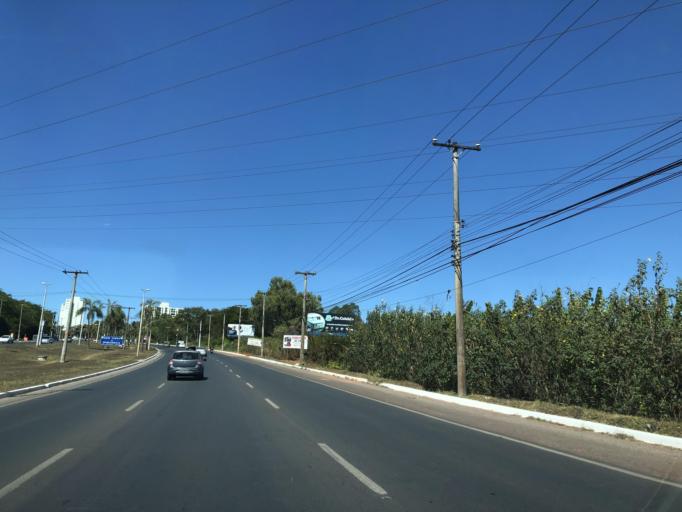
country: BR
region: Federal District
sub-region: Brasilia
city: Brasilia
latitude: -15.8442
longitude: -48.0755
